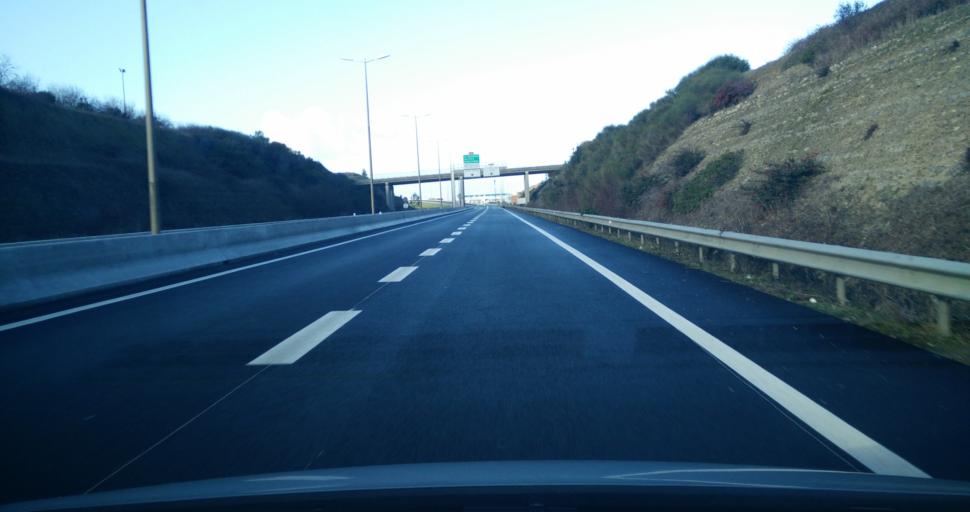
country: FR
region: Poitou-Charentes
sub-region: Departement de la Charente-Maritime
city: Nieul-sur-Mer
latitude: 46.1754
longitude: -1.2092
